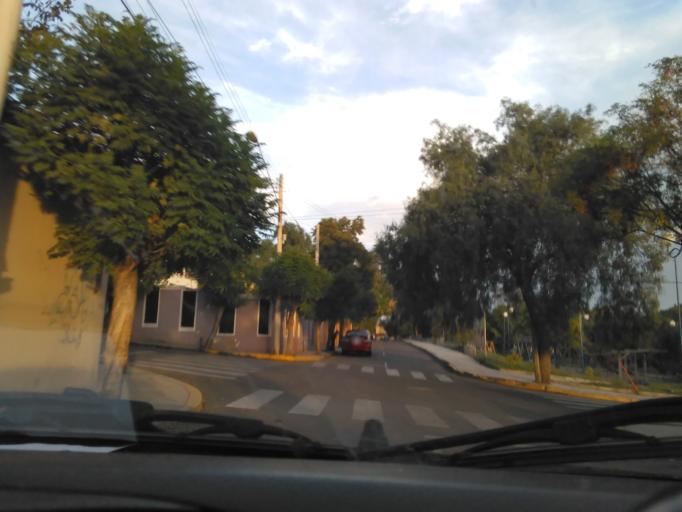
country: BO
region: Cochabamba
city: Cochabamba
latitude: -17.3725
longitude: -66.1396
